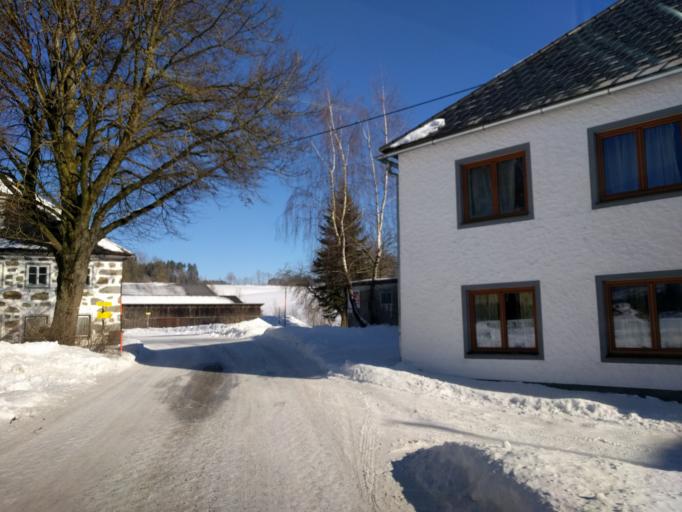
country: AT
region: Upper Austria
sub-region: Politischer Bezirk Urfahr-Umgebung
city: Zwettl an der Rodl
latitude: 48.4926
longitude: 14.2639
